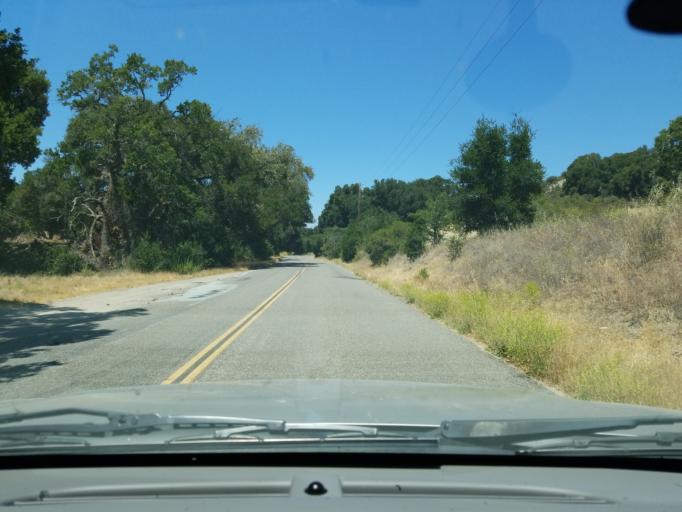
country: US
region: California
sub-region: Monterey County
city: Carmel Valley Village
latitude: 36.4311
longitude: -121.6242
